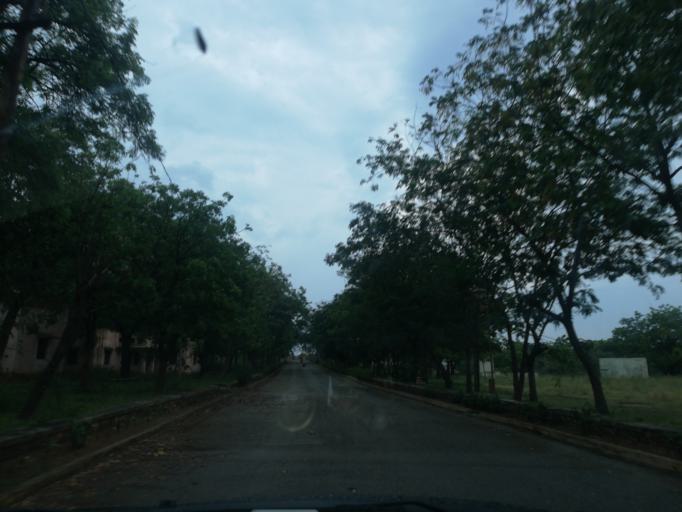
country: IN
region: Andhra Pradesh
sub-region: Guntur
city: Macherla
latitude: 16.6118
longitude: 79.2958
